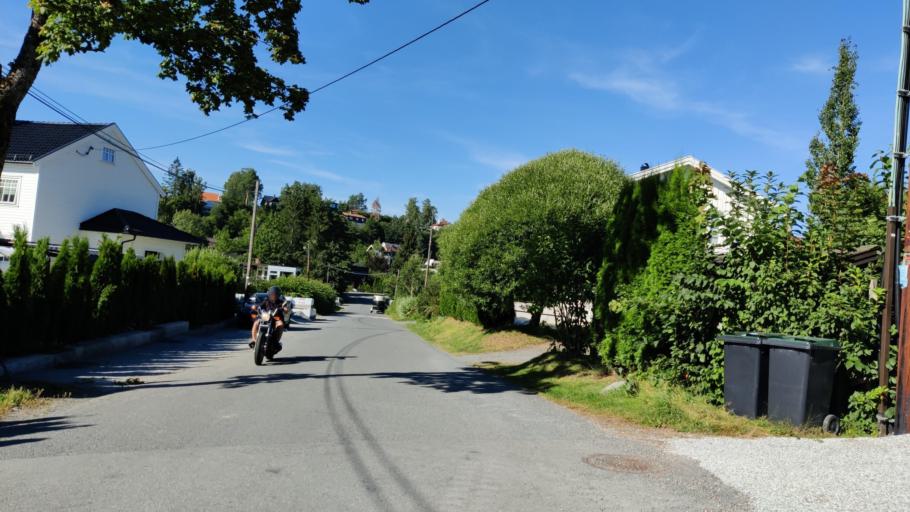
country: NO
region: Akershus
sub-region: Baerum
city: Lysaker
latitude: 59.9265
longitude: 10.6001
